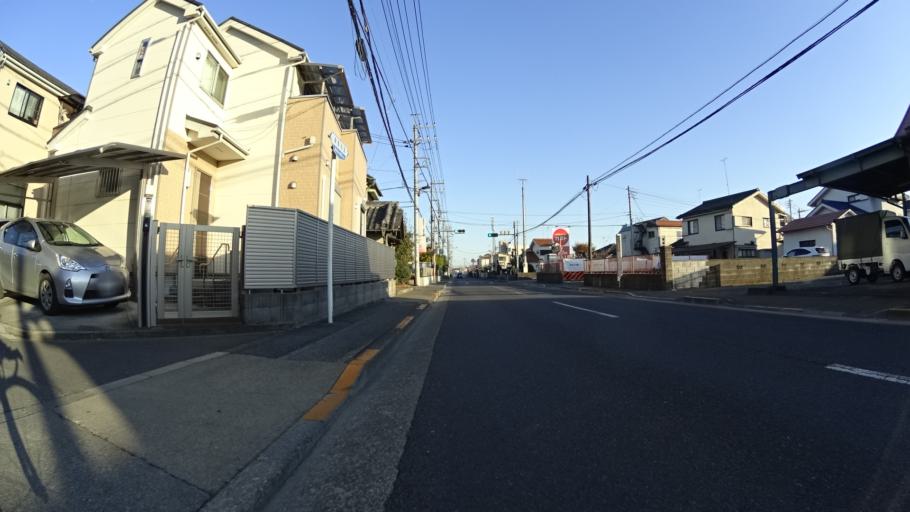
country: JP
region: Tokyo
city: Hachioji
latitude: 35.6757
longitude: 139.2899
